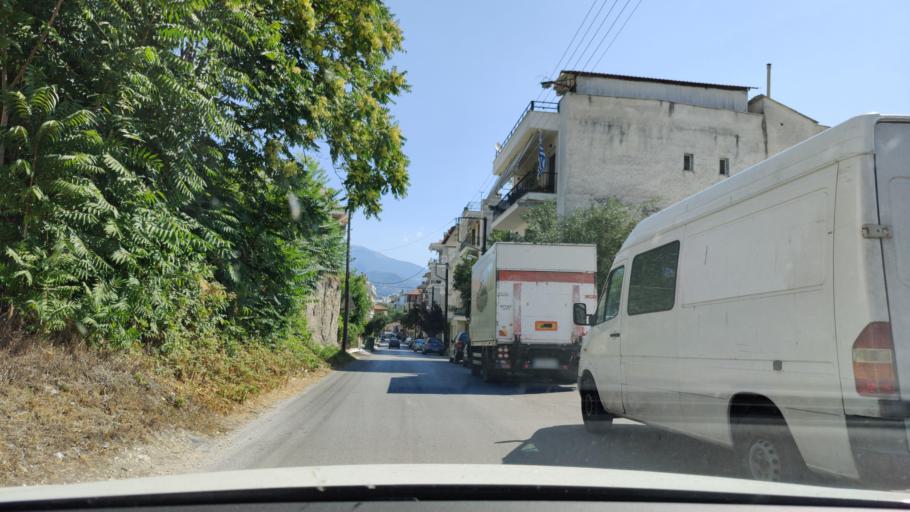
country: GR
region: Central Macedonia
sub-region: Nomos Serron
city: Serres
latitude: 41.0873
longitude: 23.5355
